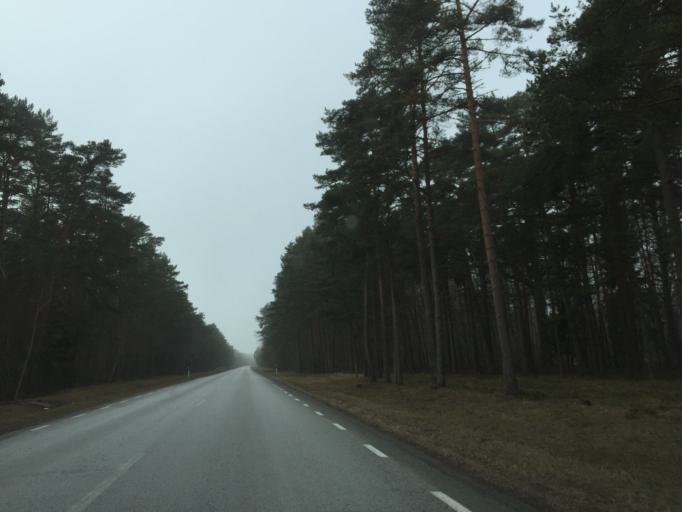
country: EE
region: Saare
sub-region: Kuressaare linn
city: Kuressaare
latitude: 58.2015
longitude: 22.2890
